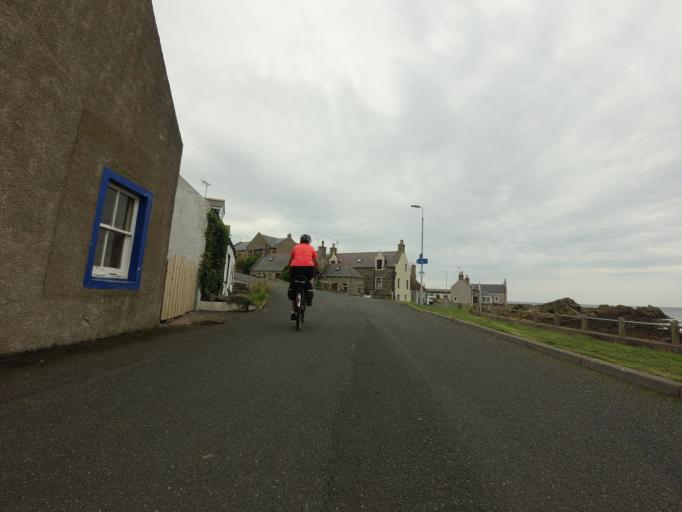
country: GB
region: Scotland
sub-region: Aberdeenshire
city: Whitehills
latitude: 57.6775
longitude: -2.5854
